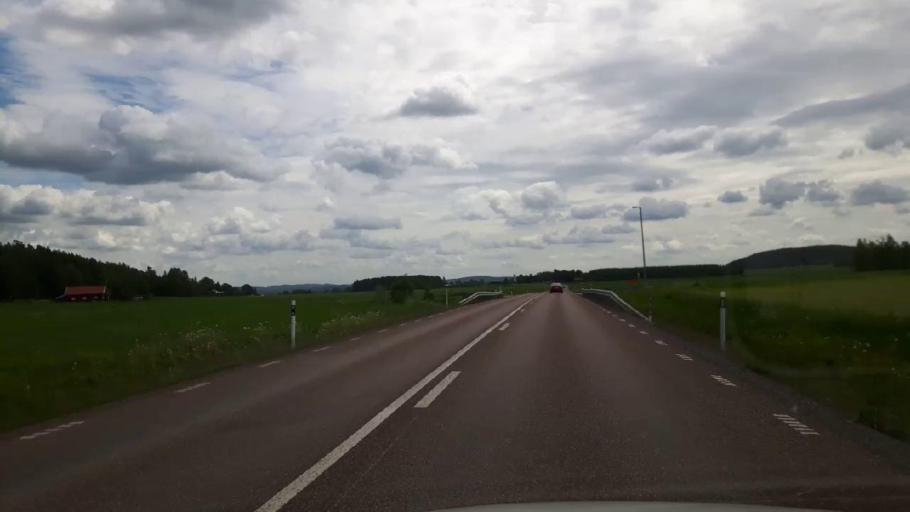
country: SE
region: Dalarna
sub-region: Hedemora Kommun
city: Hedemora
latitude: 60.3193
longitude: 15.9579
